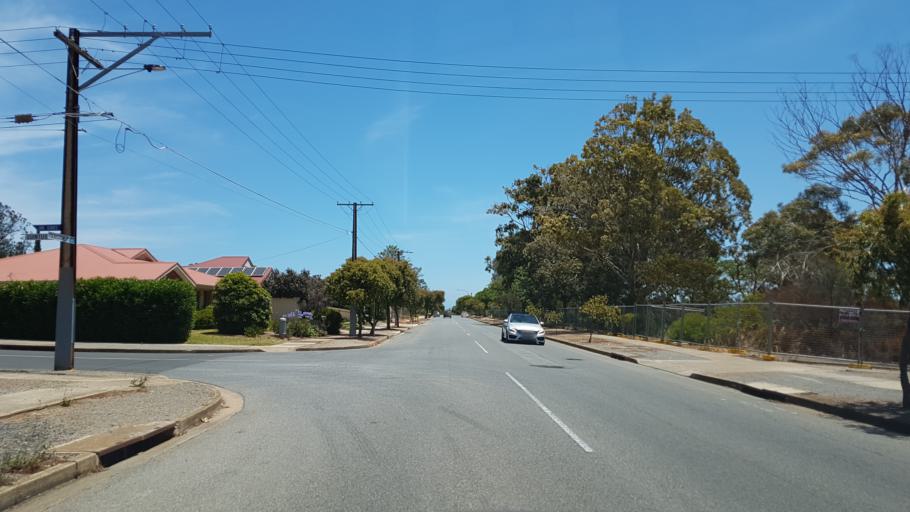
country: AU
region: South Australia
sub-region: Holdfast Bay
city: Seacliff Park
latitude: -35.0256
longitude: 138.5355
